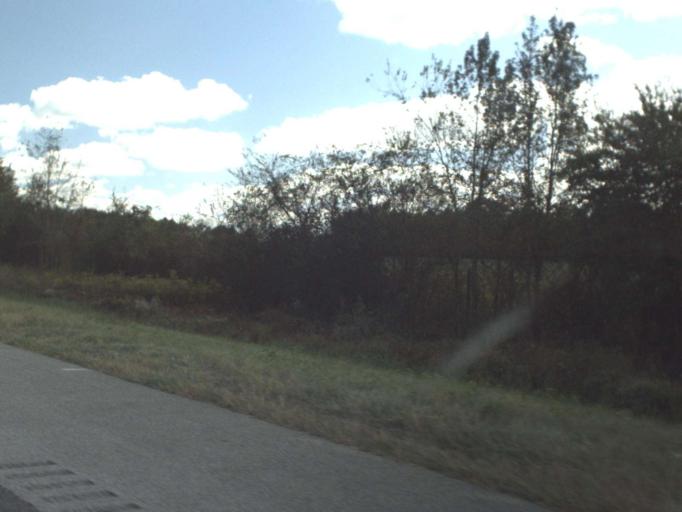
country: US
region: Florida
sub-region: Jackson County
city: Sneads
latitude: 30.6402
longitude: -84.9992
